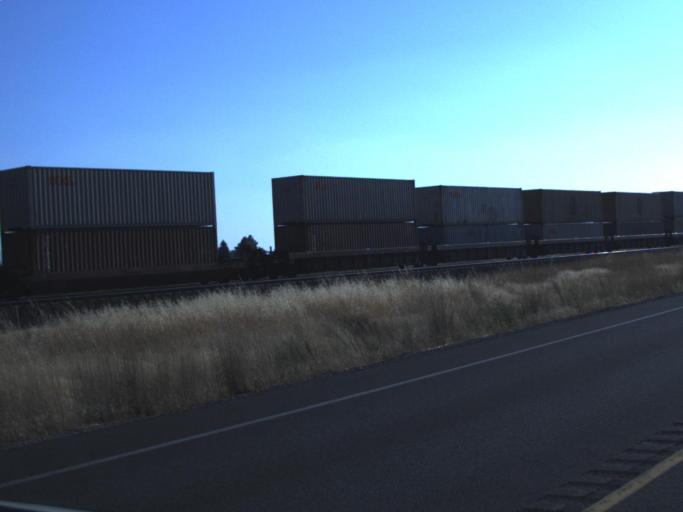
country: US
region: Washington
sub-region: Spokane County
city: Otis Orchards-East Farms
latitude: 47.7133
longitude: -117.0947
